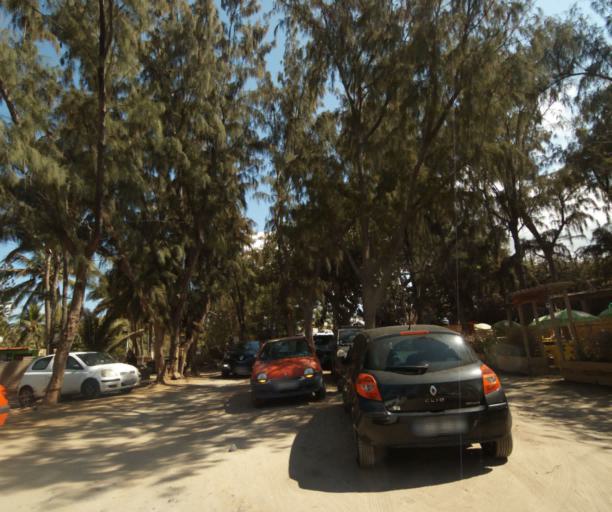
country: RE
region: Reunion
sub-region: Reunion
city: Trois-Bassins
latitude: -21.1008
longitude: 55.2438
